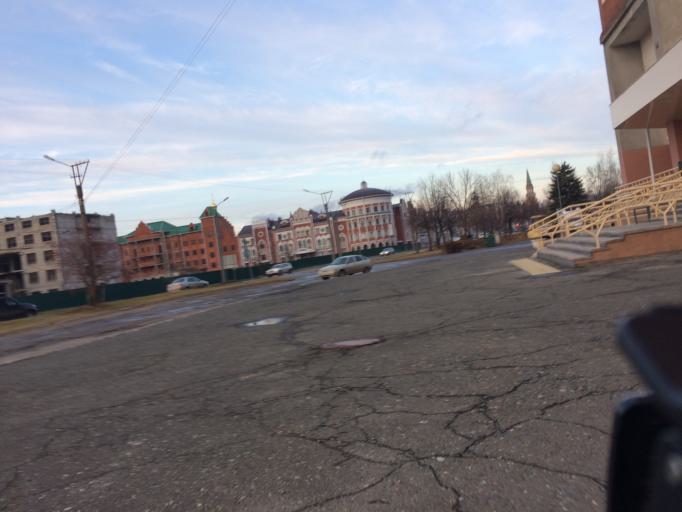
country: RU
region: Mariy-El
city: Yoshkar-Ola
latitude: 56.6281
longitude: 47.9051
